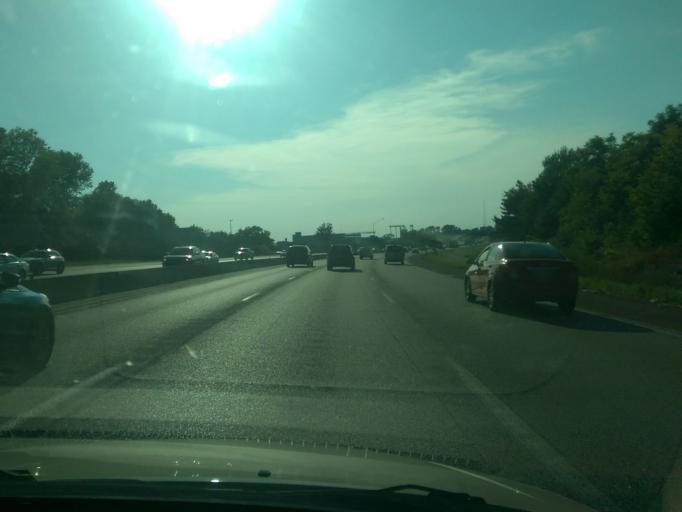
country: US
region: Missouri
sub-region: Jackson County
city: Raytown
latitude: 39.0483
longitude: -94.4657
